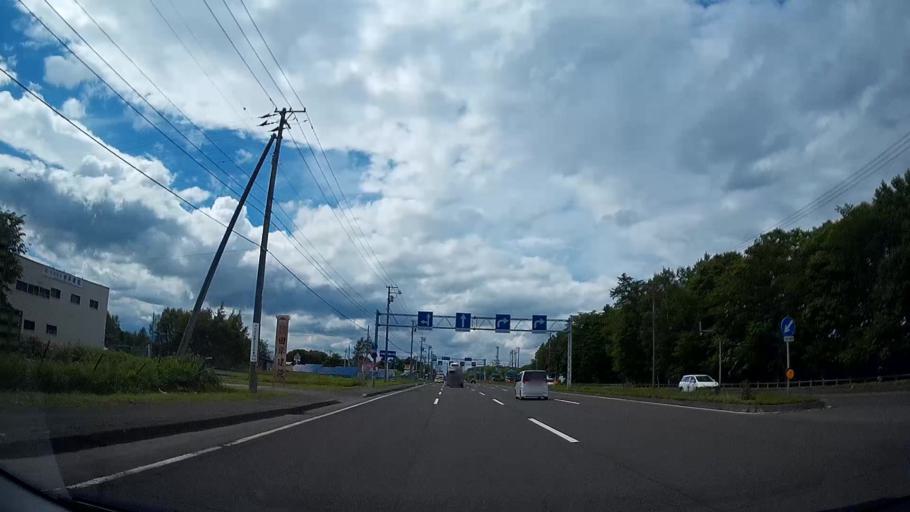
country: JP
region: Hokkaido
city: Chitose
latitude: 42.8601
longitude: 141.6017
